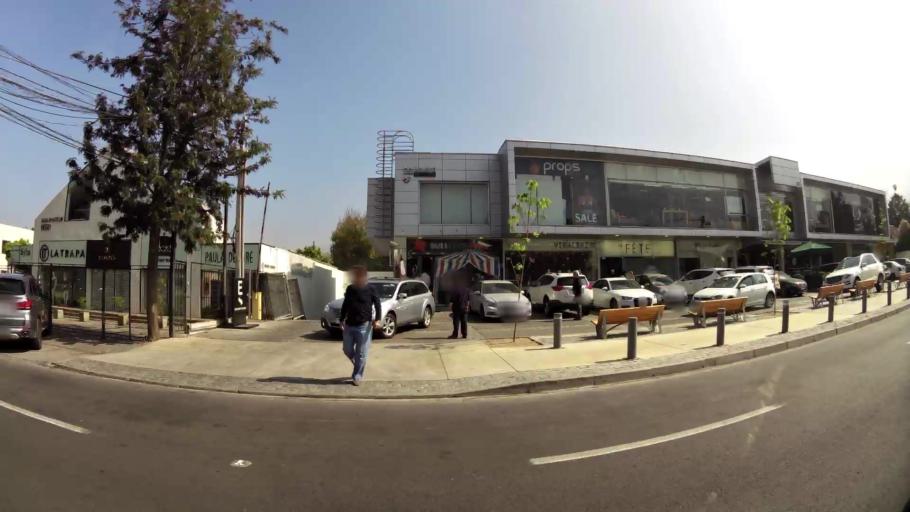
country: CL
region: Santiago Metropolitan
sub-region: Provincia de Santiago
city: Villa Presidente Frei, Nunoa, Santiago, Chile
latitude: -33.3809
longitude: -70.5709
